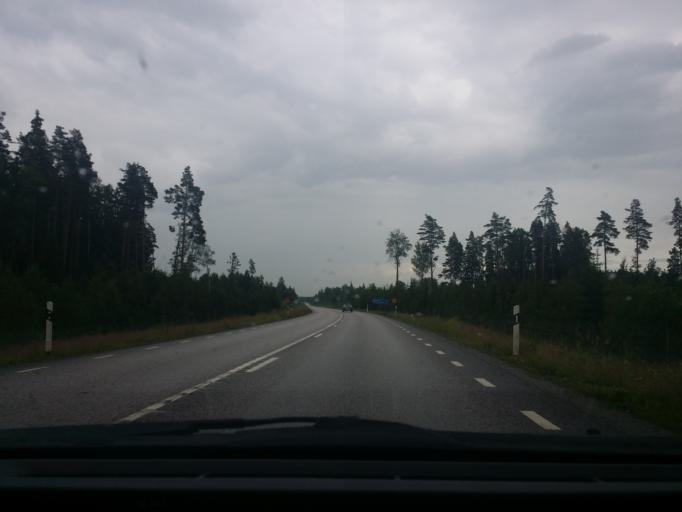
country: SE
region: OErebro
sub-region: Lindesbergs Kommun
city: Frovi
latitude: 59.4779
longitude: 15.3836
